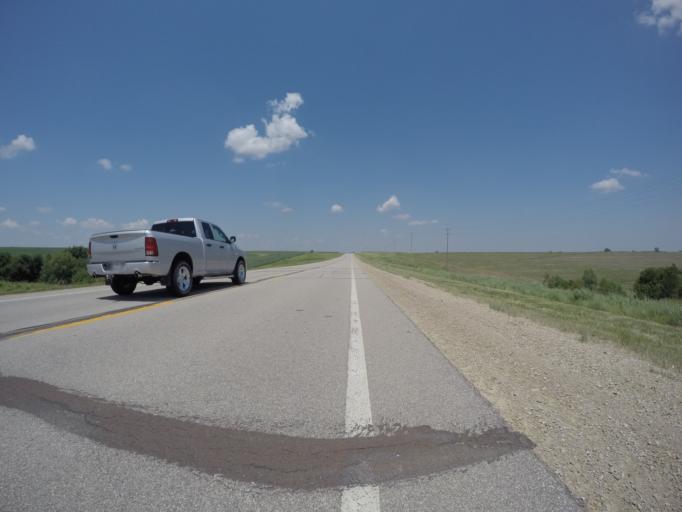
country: US
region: Kansas
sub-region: Doniphan County
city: Troy
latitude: 39.7447
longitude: -95.1438
